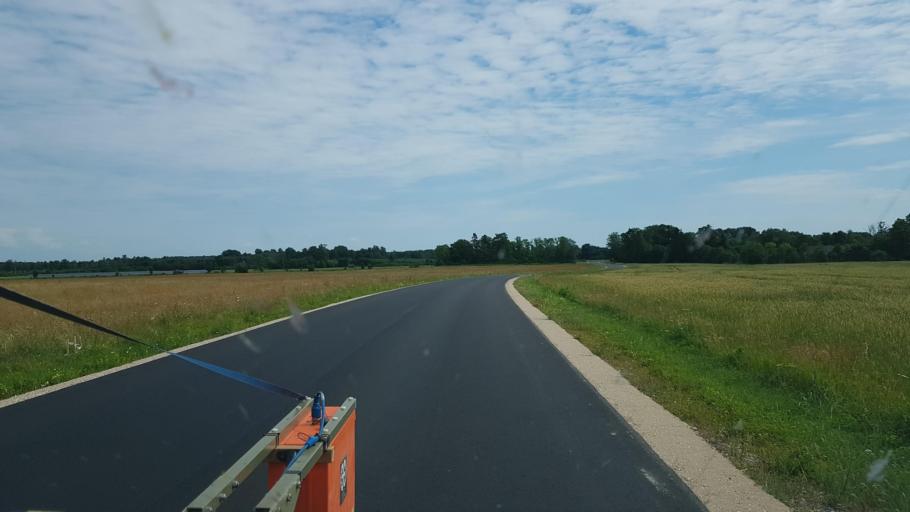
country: EE
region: Paernumaa
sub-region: Halinga vald
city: Parnu-Jaagupi
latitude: 58.6197
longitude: 24.3088
